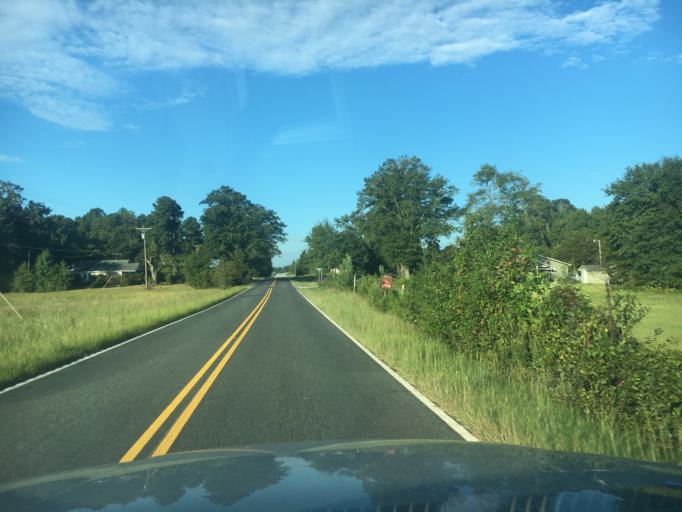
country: US
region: South Carolina
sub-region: Spartanburg County
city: Woodruff
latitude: 34.6193
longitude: -82.0790
